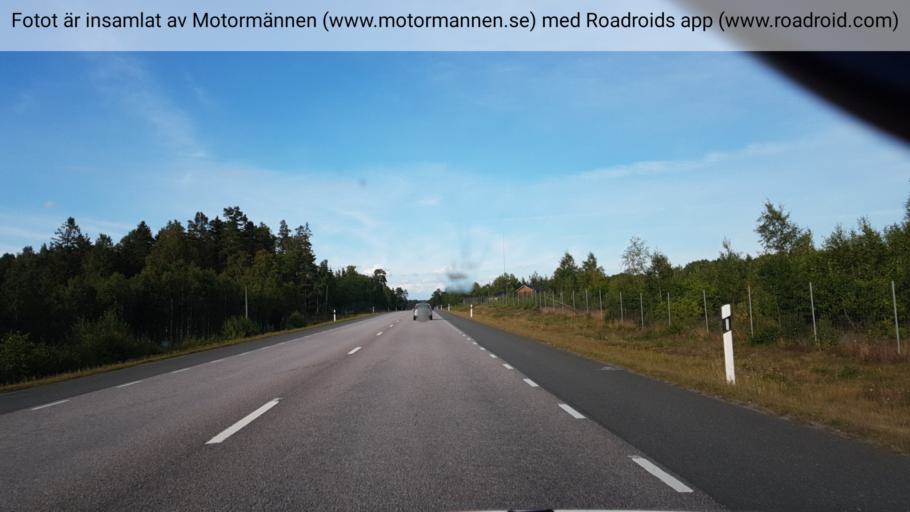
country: SE
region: Vaestra Goetaland
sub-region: Gotene Kommun
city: Goetene
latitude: 58.5625
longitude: 13.5738
